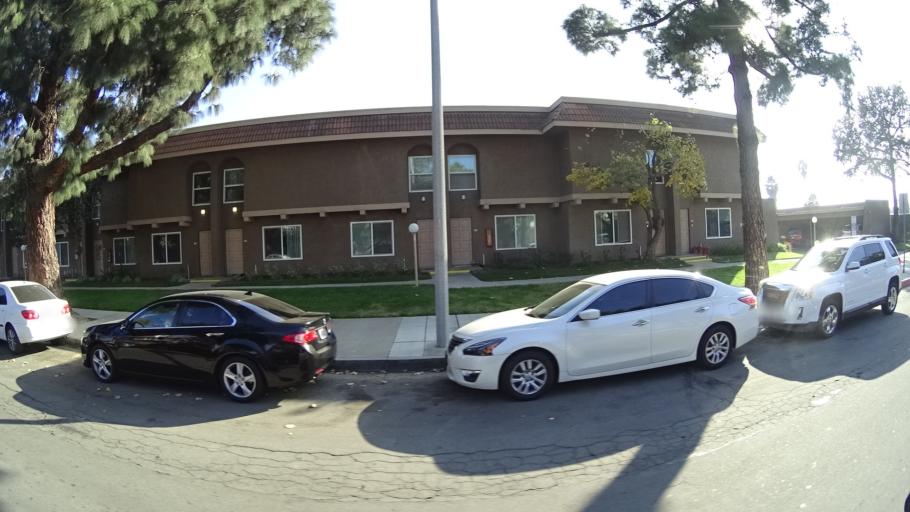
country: US
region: California
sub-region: Orange County
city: Placentia
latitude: 33.8449
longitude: -117.8622
